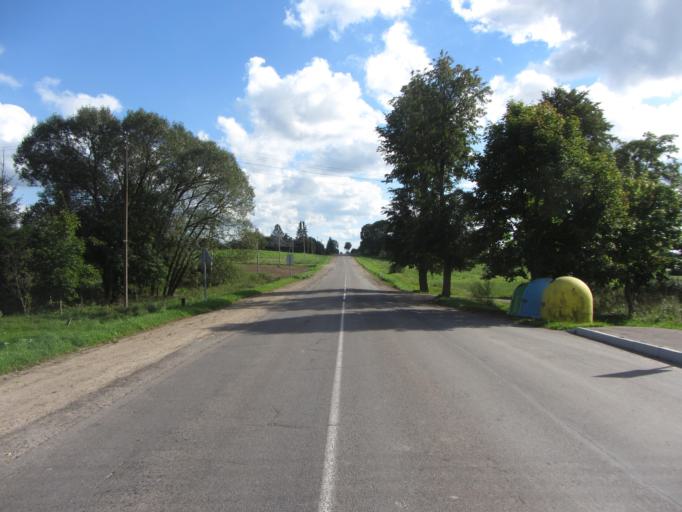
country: LT
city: Vilkija
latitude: 55.0713
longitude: 23.5493
